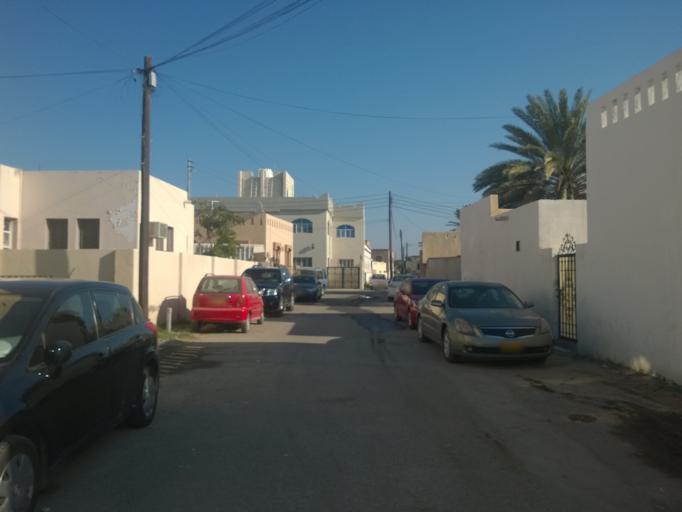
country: OM
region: Muhafazat Masqat
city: As Sib al Jadidah
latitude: 23.6682
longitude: 58.1875
